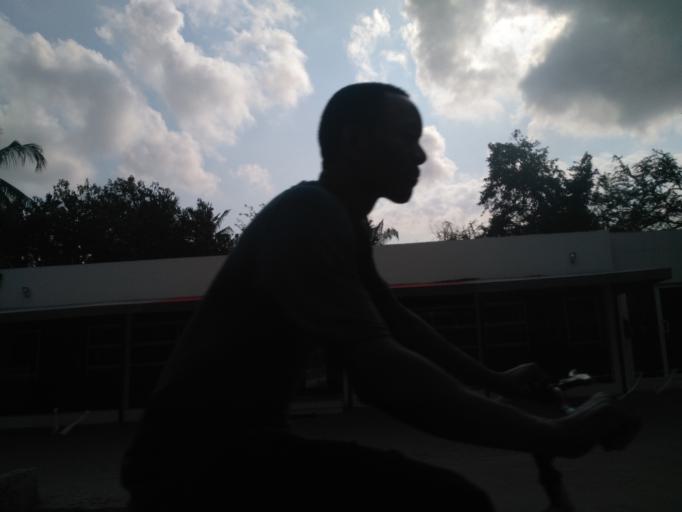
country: TZ
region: Dar es Salaam
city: Magomeni
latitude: -6.7489
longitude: 39.2412
